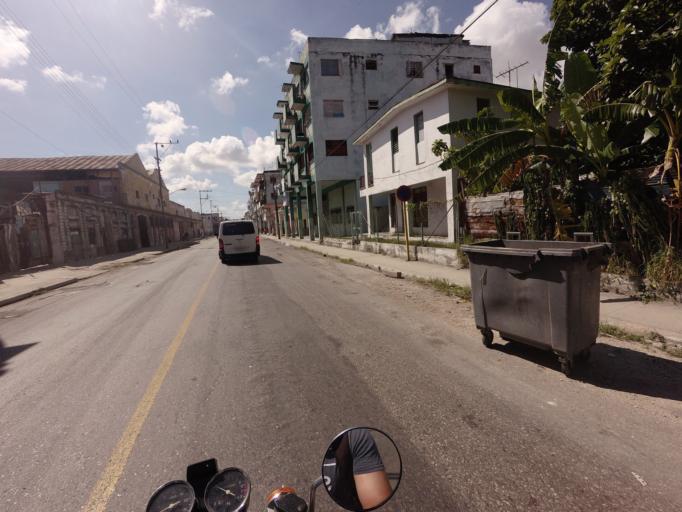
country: TM
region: Balkan
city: Gumdag
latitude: 38.8432
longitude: 54.1832
